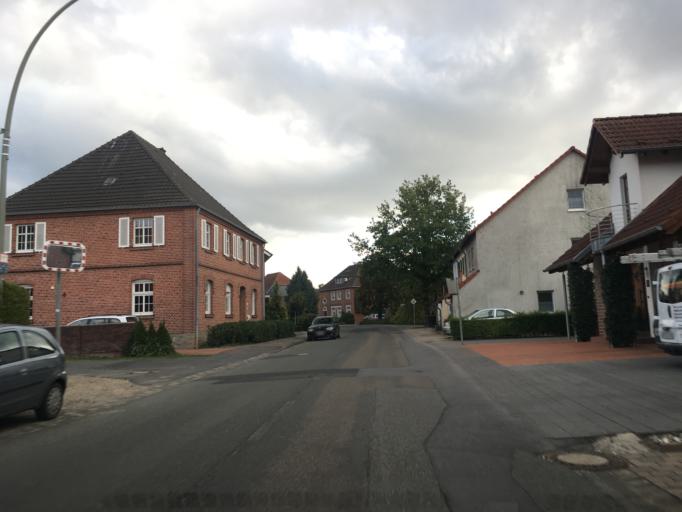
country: DE
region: North Rhine-Westphalia
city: Ludinghausen
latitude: 51.7626
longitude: 7.3893
